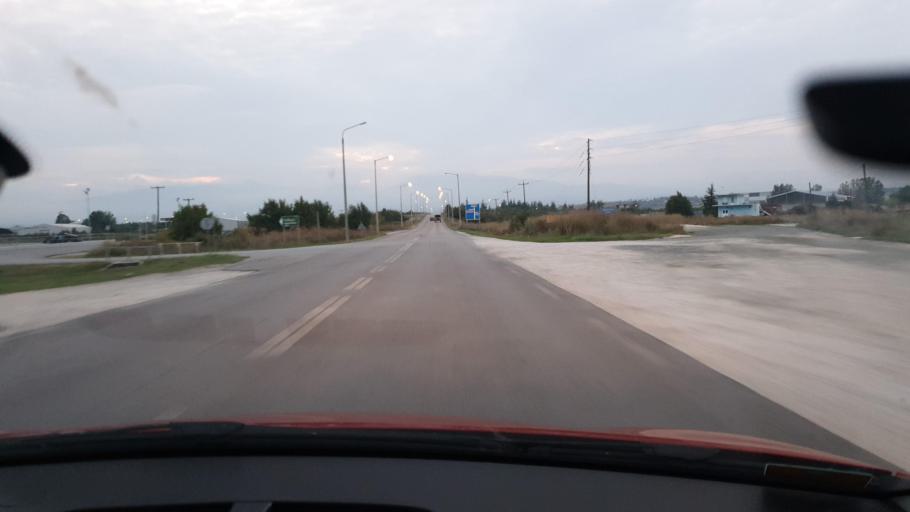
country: GR
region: Central Macedonia
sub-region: Nomos Kilkis
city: Polykastro
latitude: 40.9903
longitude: 22.6108
